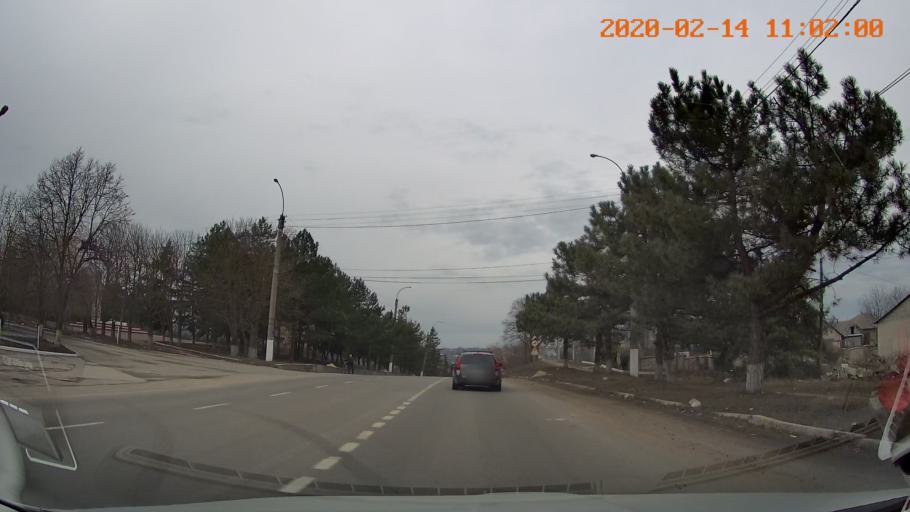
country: MD
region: Raionul Edinet
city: Edinet
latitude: 48.1626
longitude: 27.3240
